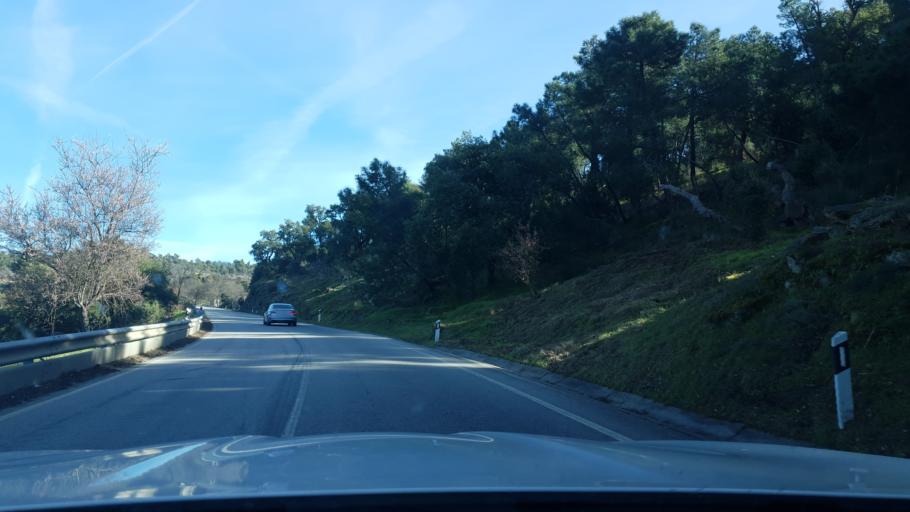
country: PT
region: Braganca
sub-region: Torre de Moncorvo
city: Torre de Moncorvo
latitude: 41.1810
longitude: -7.0260
